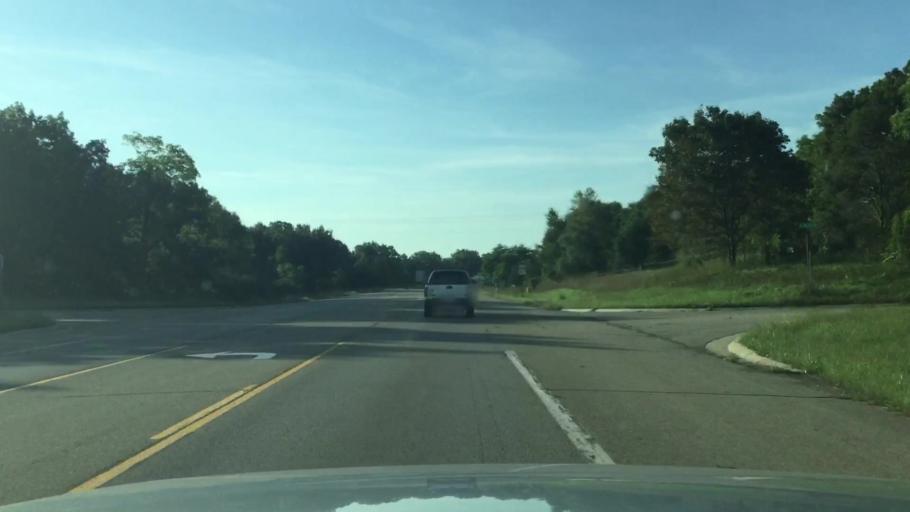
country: US
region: Michigan
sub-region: Jackson County
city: Vandercook Lake
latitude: 42.1829
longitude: -84.3669
